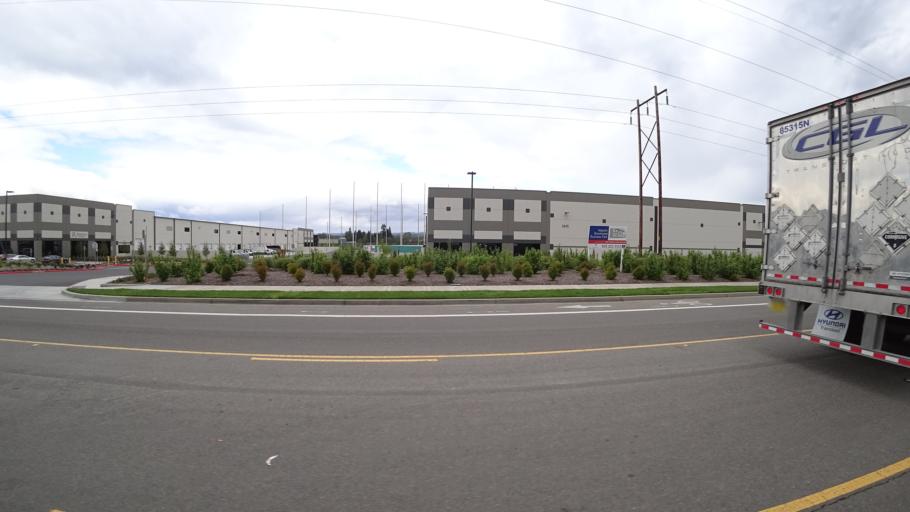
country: US
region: Oregon
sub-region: Washington County
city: Rockcreek
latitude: 45.5569
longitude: -122.9225
